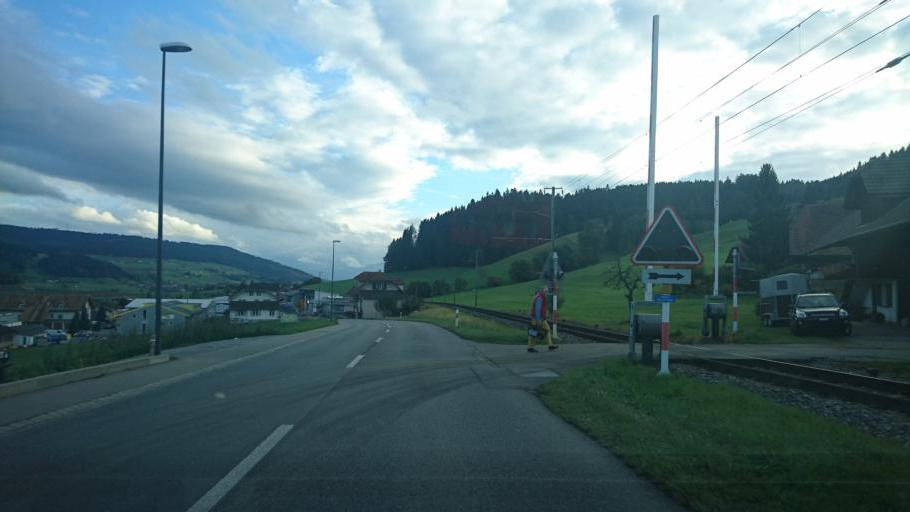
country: CH
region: Bern
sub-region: Bern-Mittelland District
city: Biglen
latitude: 46.9022
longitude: 7.6335
